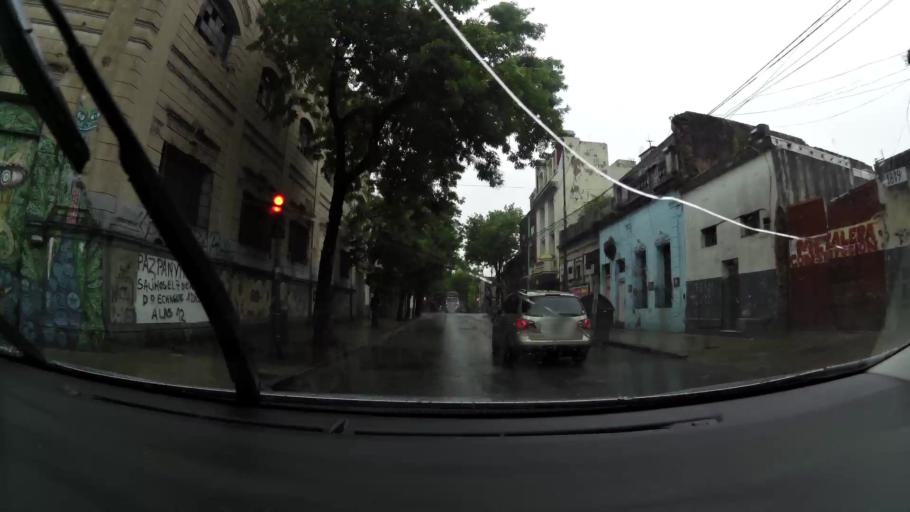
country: AR
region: Buenos Aires F.D.
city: Buenos Aires
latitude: -34.6292
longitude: -58.3842
